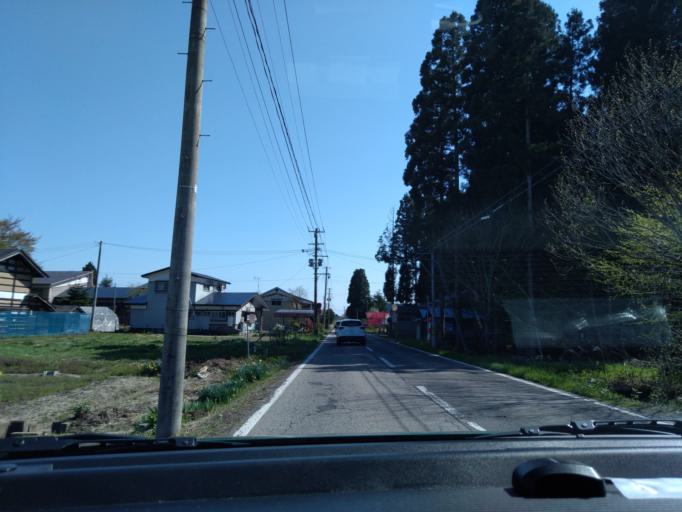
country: JP
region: Akita
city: Kakunodatemachi
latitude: 39.5480
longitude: 140.5858
